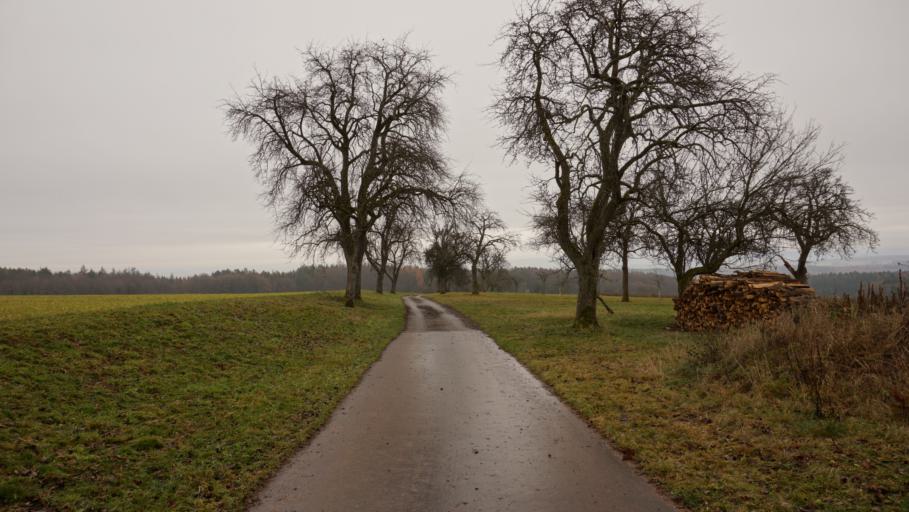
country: DE
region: Baden-Wuerttemberg
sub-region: Karlsruhe Region
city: Fahrenbach
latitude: 49.4429
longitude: 9.1091
